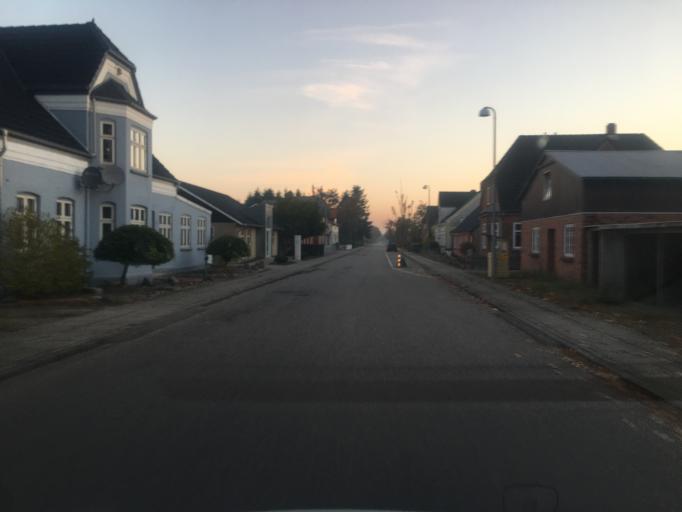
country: DE
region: Schleswig-Holstein
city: Bramstedtlund
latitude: 54.9427
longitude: 9.0874
